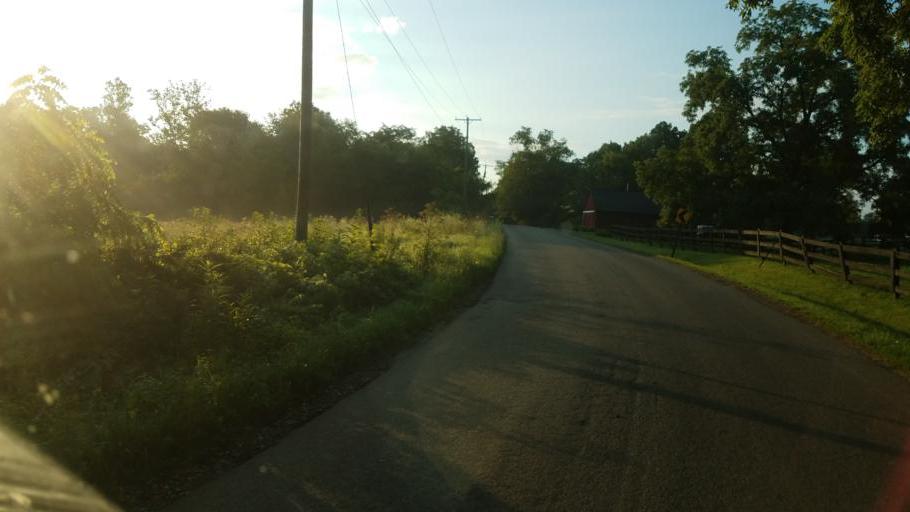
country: US
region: Ohio
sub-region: Morrow County
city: Mount Gilead
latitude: 40.5584
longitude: -82.6911
